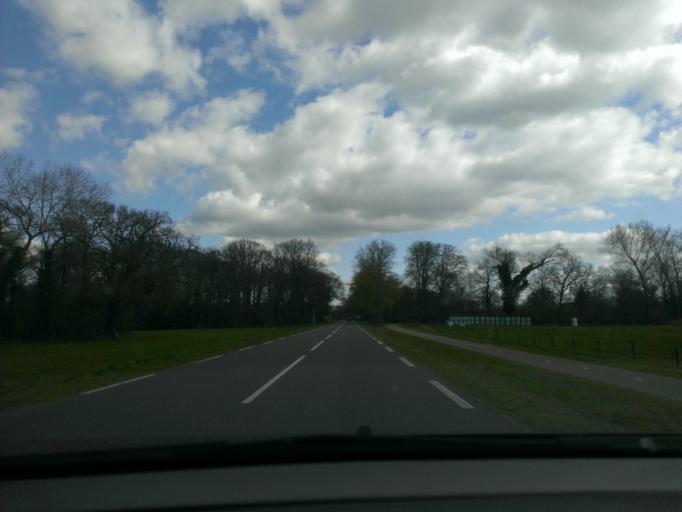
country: NL
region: Overijssel
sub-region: Gemeente Borne
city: Borne
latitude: 52.3056
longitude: 6.7197
